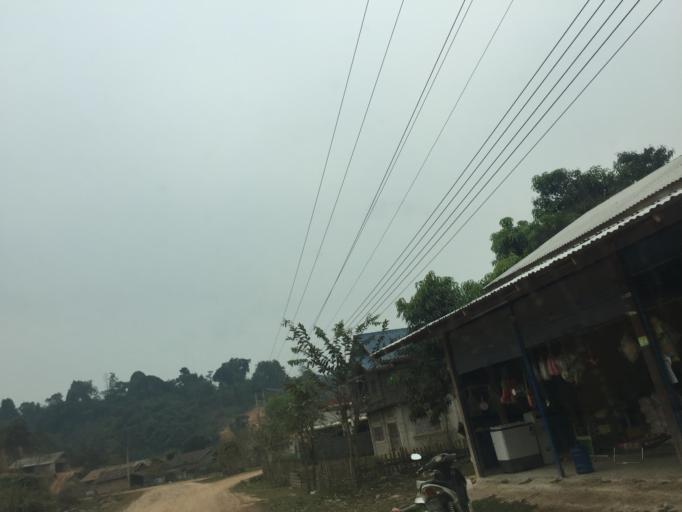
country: TH
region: Loei
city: Pak Chom
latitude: 18.5451
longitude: 101.6028
